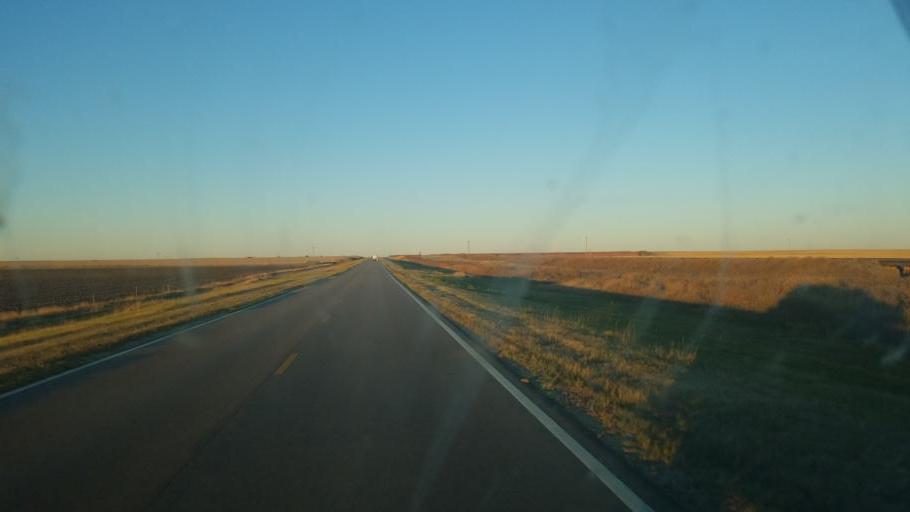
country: US
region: Kansas
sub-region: Wallace County
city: Sharon Springs
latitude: 38.8792
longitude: -101.9218
